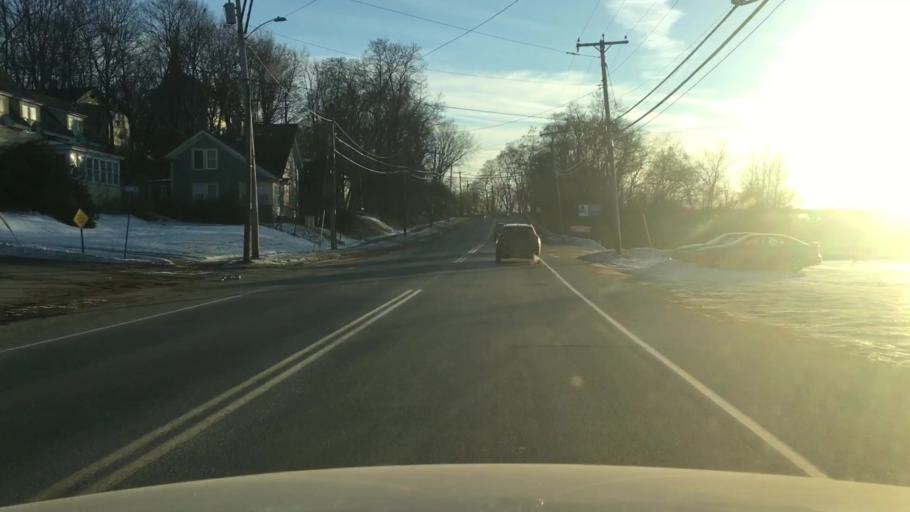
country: US
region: Maine
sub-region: Penobscot County
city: Brewer
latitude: 44.7902
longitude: -68.7693
